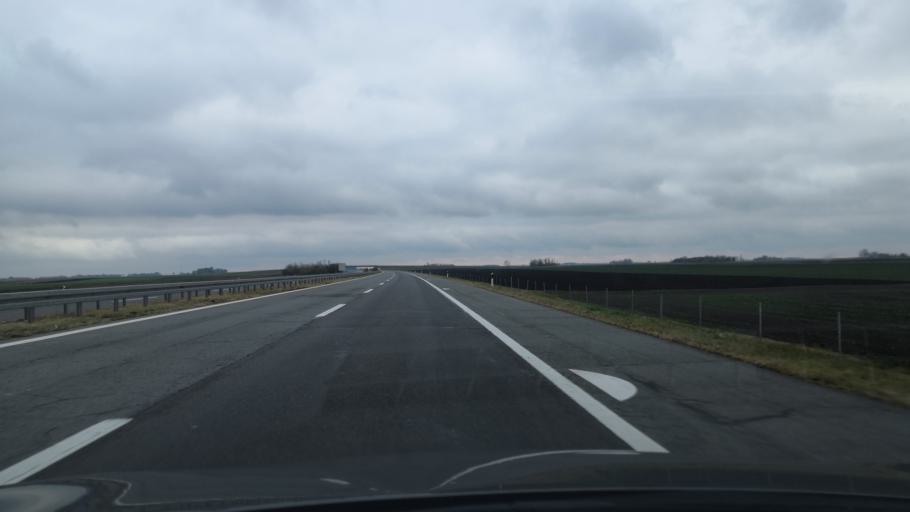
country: RS
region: Autonomna Pokrajina Vojvodina
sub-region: Severnobacki Okrug
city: Backa Topola
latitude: 45.8118
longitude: 19.6875
